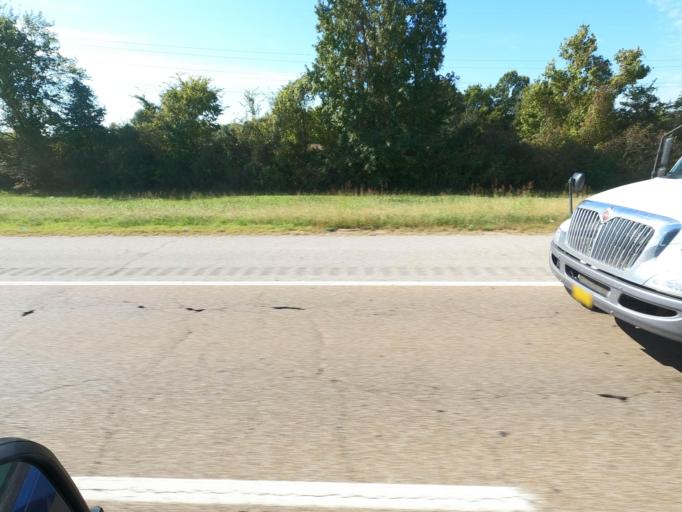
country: US
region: Tennessee
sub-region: Shelby County
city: Millington
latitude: 35.3286
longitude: -89.8897
